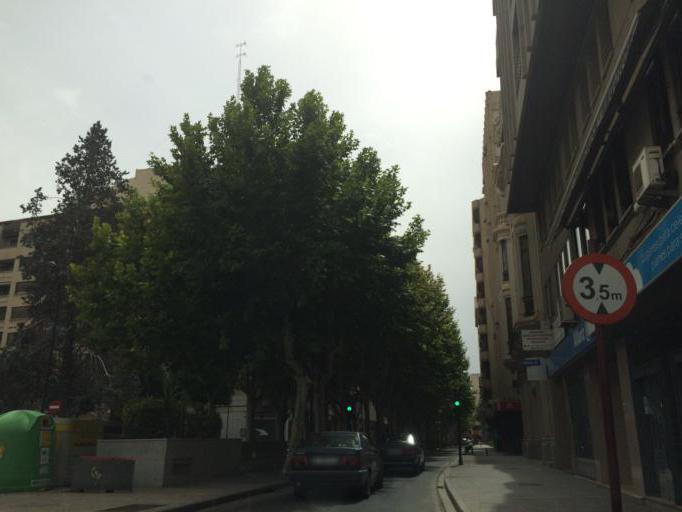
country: ES
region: Castille-La Mancha
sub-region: Provincia de Albacete
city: Albacete
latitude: 38.9970
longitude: -1.8524
